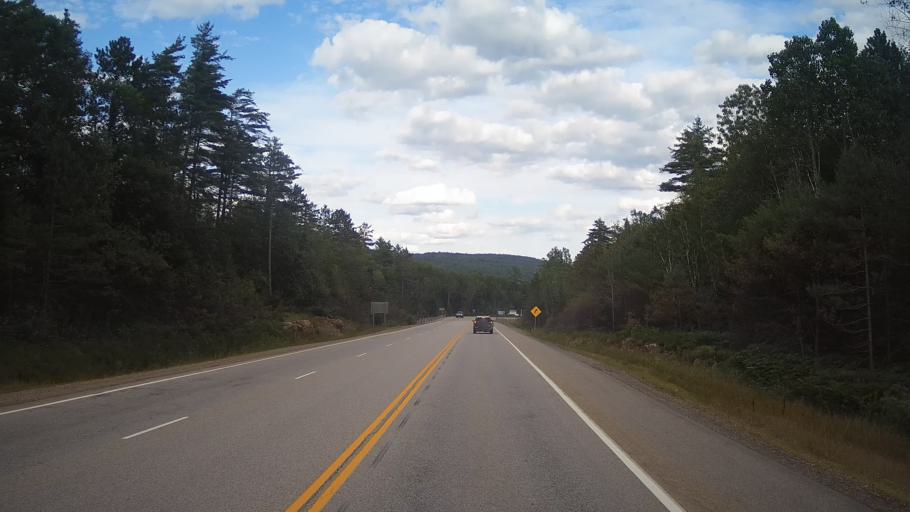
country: CA
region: Ontario
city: Mattawa
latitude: 46.2834
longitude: -78.4021
